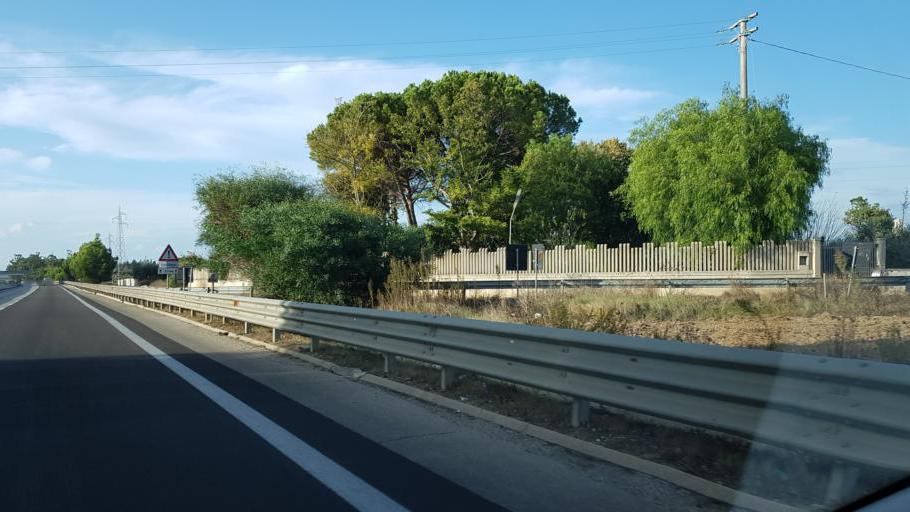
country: IT
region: Apulia
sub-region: Provincia di Brindisi
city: Francavilla Fontana
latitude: 40.5333
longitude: 17.6169
